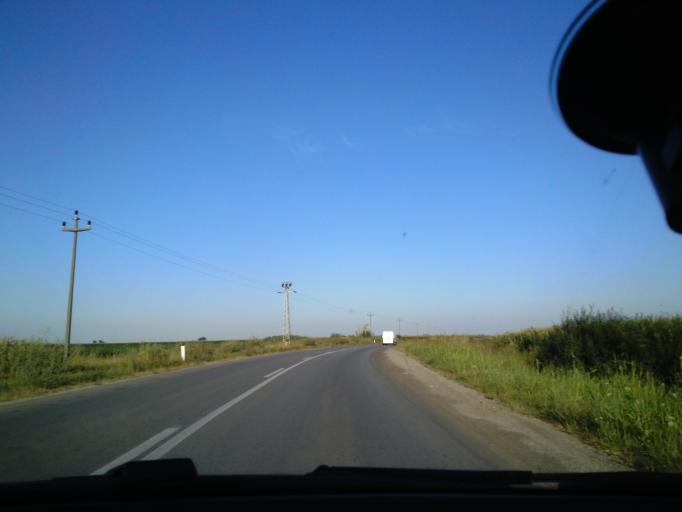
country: RS
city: Obrovac
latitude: 45.4097
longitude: 19.4121
